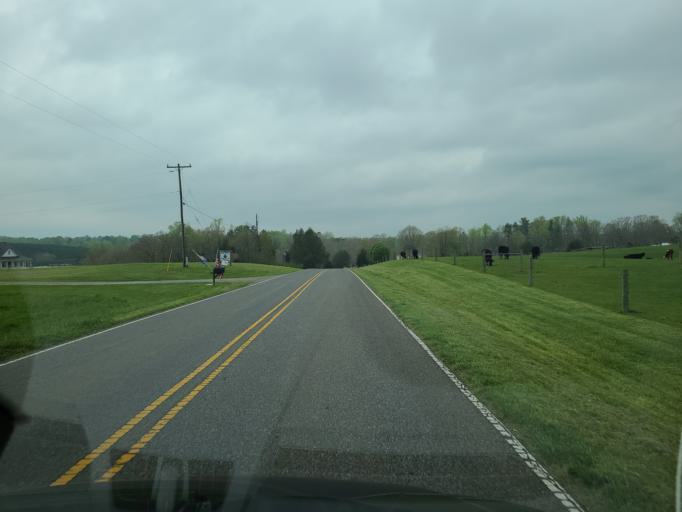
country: US
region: North Carolina
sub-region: Gaston County
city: Cherryville
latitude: 35.4286
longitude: -81.4689
